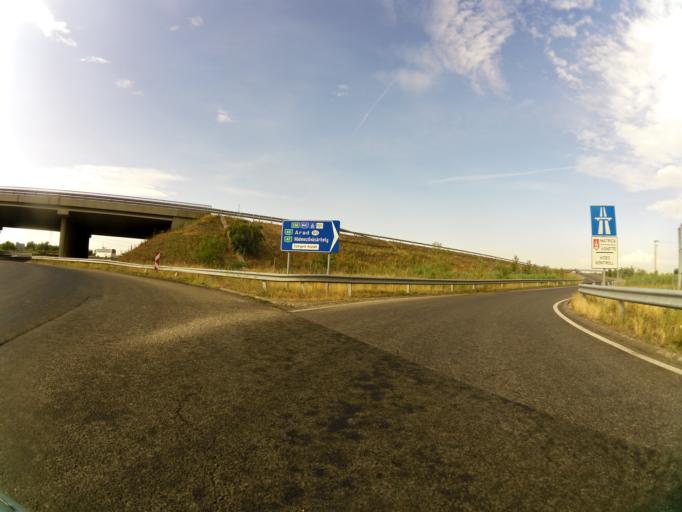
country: HU
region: Csongrad
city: Szatymaz
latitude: 46.2931
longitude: 20.0827
